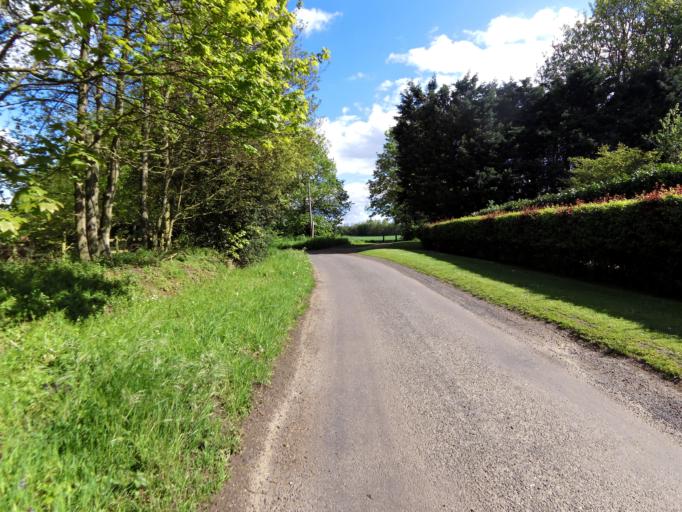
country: GB
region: England
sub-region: Suffolk
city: Thurston
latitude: 52.2419
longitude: 0.8279
